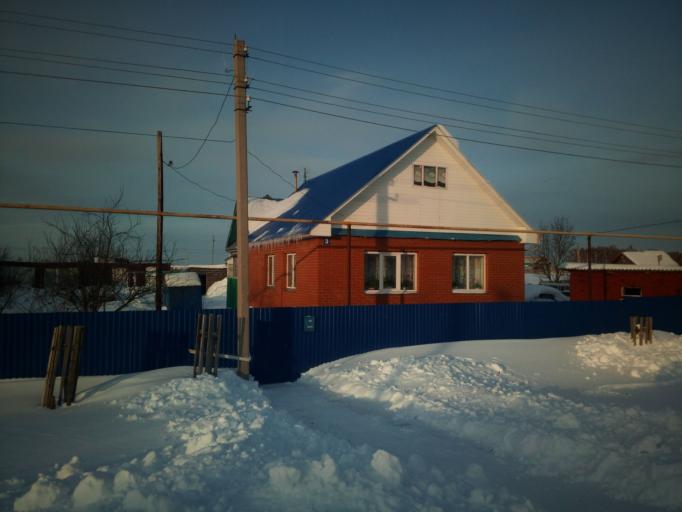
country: RU
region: Bashkortostan
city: Amzya
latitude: 56.1668
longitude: 54.3787
